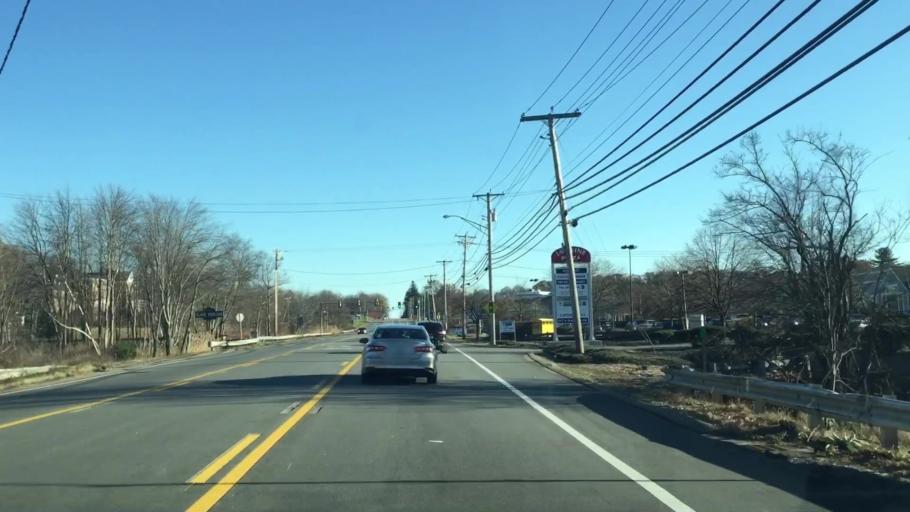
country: US
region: Massachusetts
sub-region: Essex County
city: Andover
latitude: 42.6618
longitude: -71.1103
